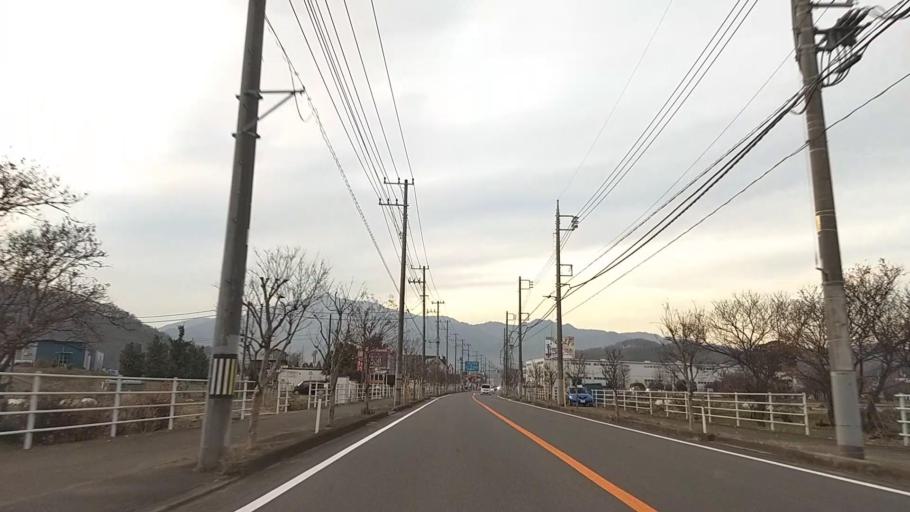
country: JP
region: Kanagawa
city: Atsugi
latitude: 35.4302
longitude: 139.3321
